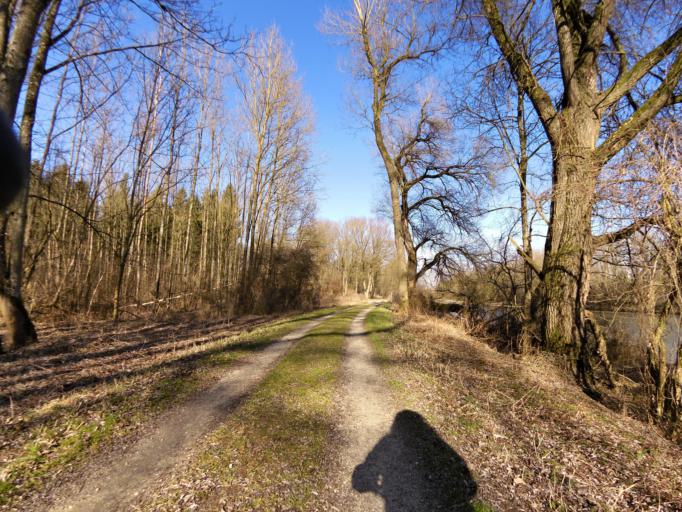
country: DE
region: Bavaria
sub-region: Lower Bavaria
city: Eching
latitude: 48.5107
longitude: 12.0744
